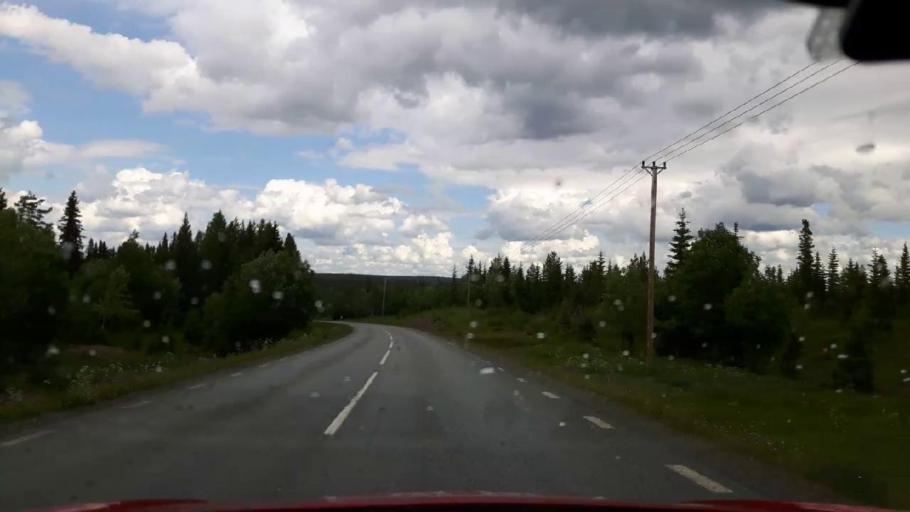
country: SE
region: Jaemtland
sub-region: Krokoms Kommun
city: Krokom
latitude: 63.5447
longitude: 14.2754
